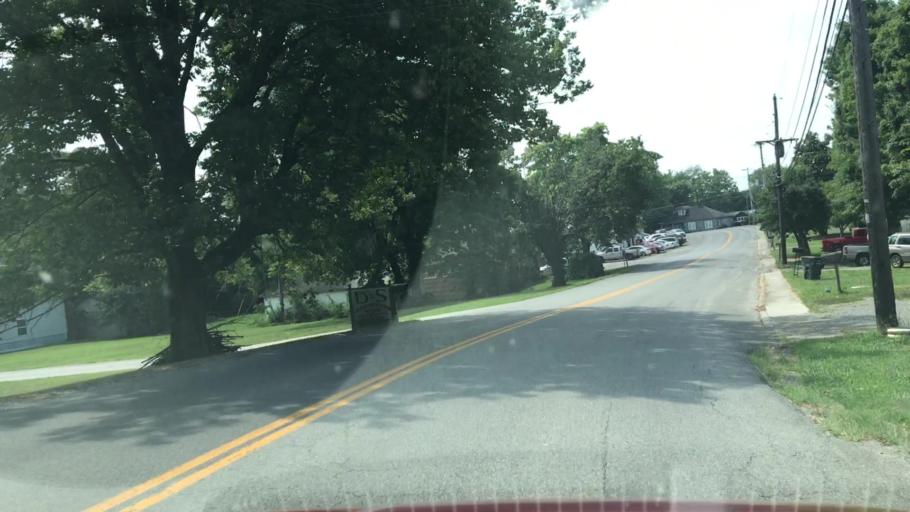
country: US
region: Kentucky
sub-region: Monroe County
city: Tompkinsville
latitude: 36.7068
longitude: -85.6997
